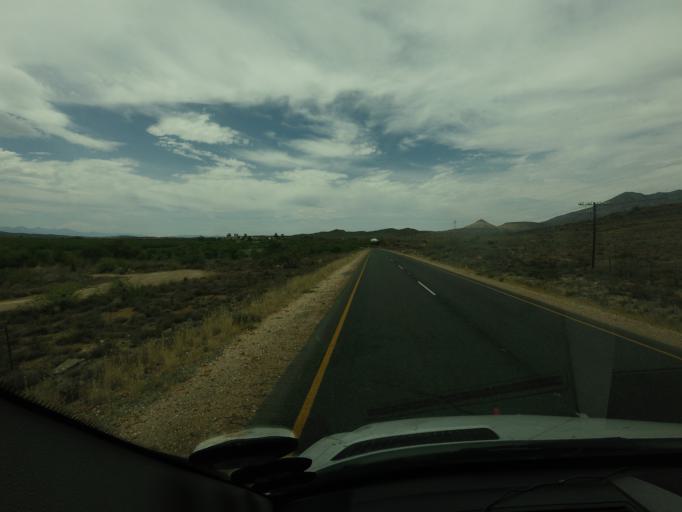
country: ZA
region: Western Cape
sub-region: Overberg District Municipality
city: Swellendam
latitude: -33.8506
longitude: 20.8454
